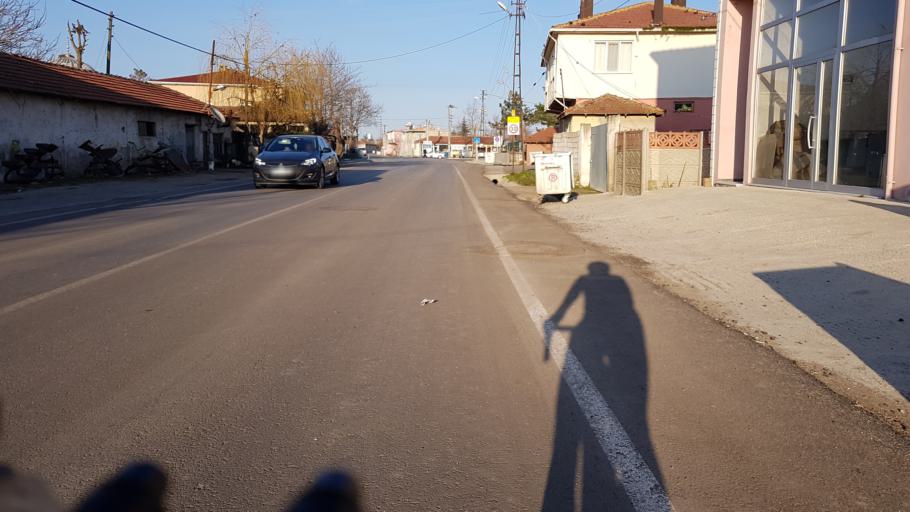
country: TR
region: Tekirdag
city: Beyazkoy
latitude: 41.3048
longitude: 27.7874
